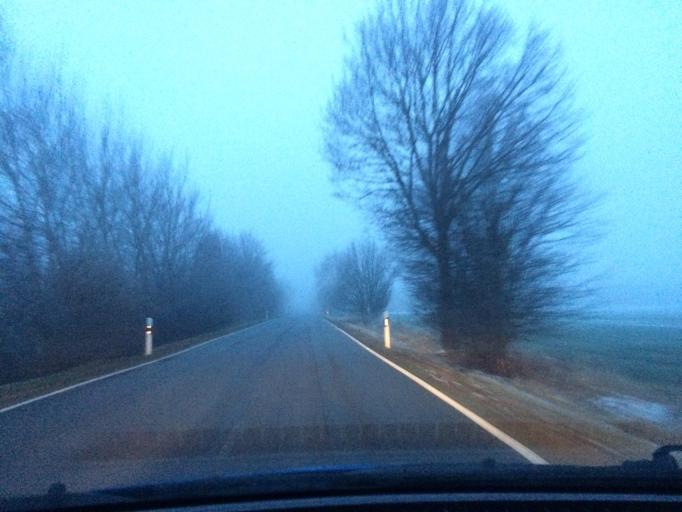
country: DE
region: Schleswig-Holstein
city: Wiershop
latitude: 53.4478
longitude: 10.4517
